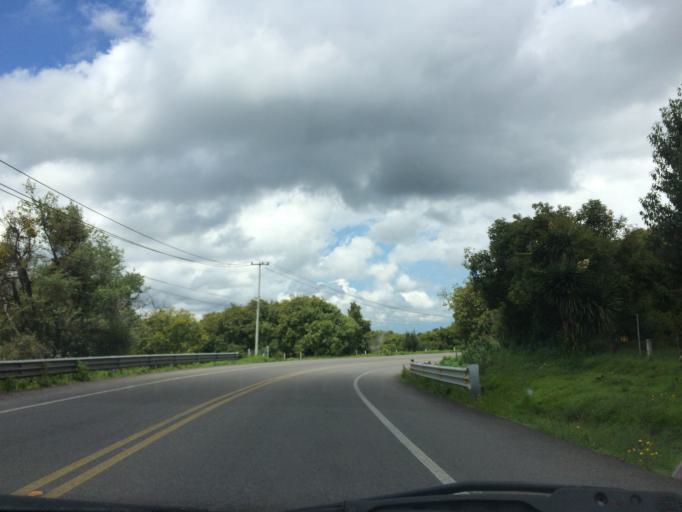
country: MX
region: Michoacan
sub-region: Uruapan
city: Santa Ana Zirosto
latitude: 19.5516
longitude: -102.3019
